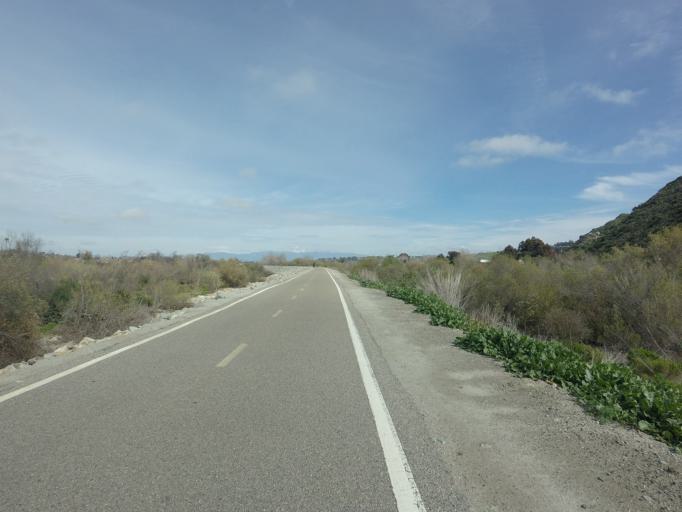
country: US
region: California
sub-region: San Diego County
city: Camp Pendleton South
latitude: 33.2142
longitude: -117.3637
